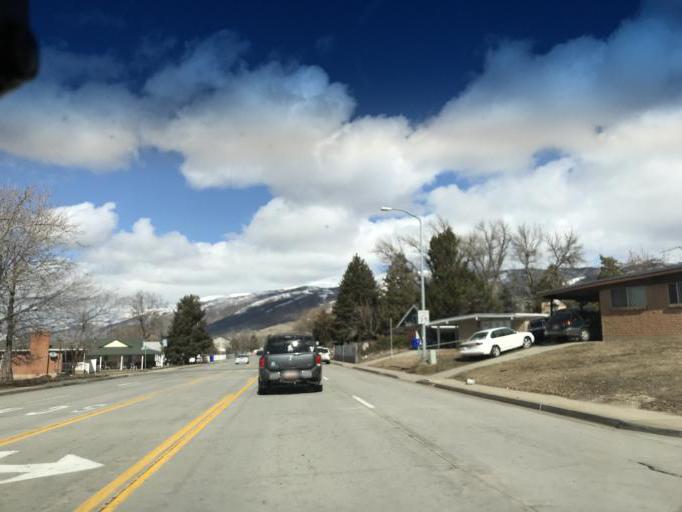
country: US
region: Utah
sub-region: Davis County
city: Woods Cross
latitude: 40.8721
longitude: -111.8762
